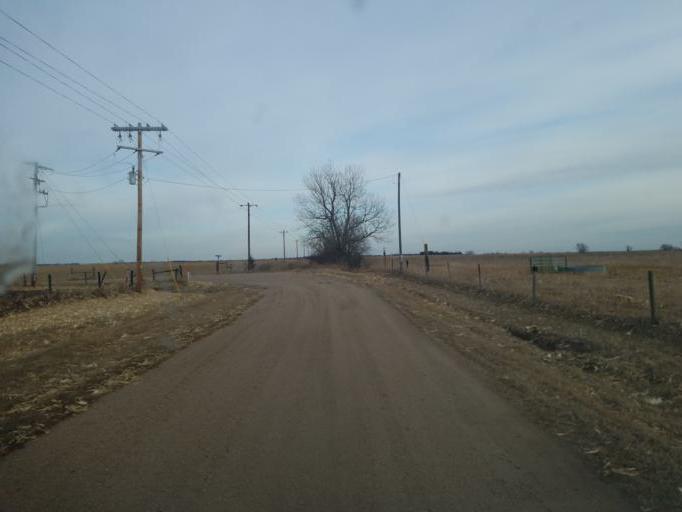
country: US
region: Nebraska
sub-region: Holt County
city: O'Neill
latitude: 42.4369
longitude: -98.3061
